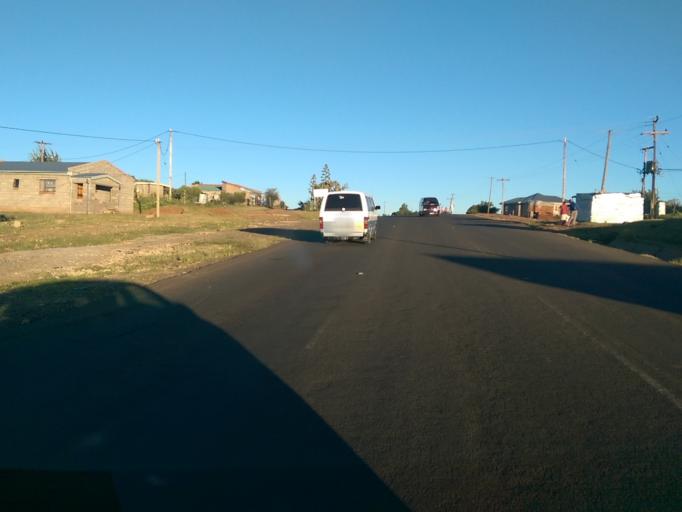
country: LS
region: Maseru
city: Maseru
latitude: -29.4086
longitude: 27.5799
